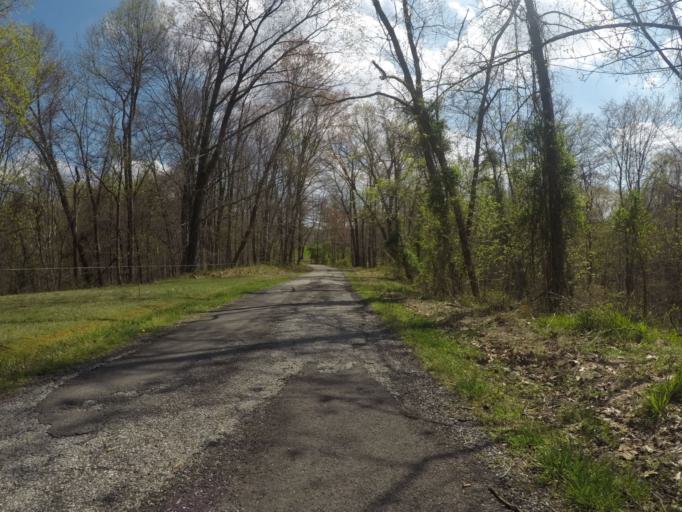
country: US
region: West Virginia
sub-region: Wayne County
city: Ceredo
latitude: 38.3887
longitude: -82.5441
